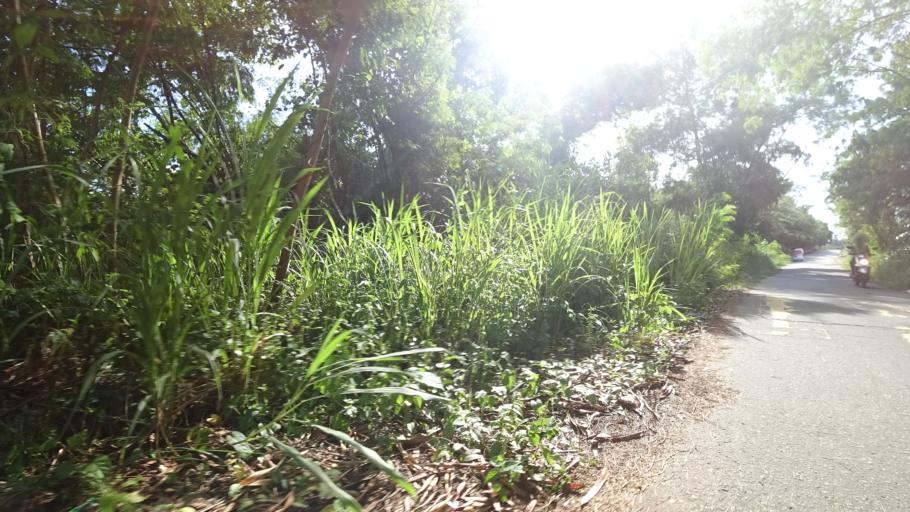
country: BN
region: Brunei and Muara
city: Bandar Seri Begawan
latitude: 4.9484
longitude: 114.8378
